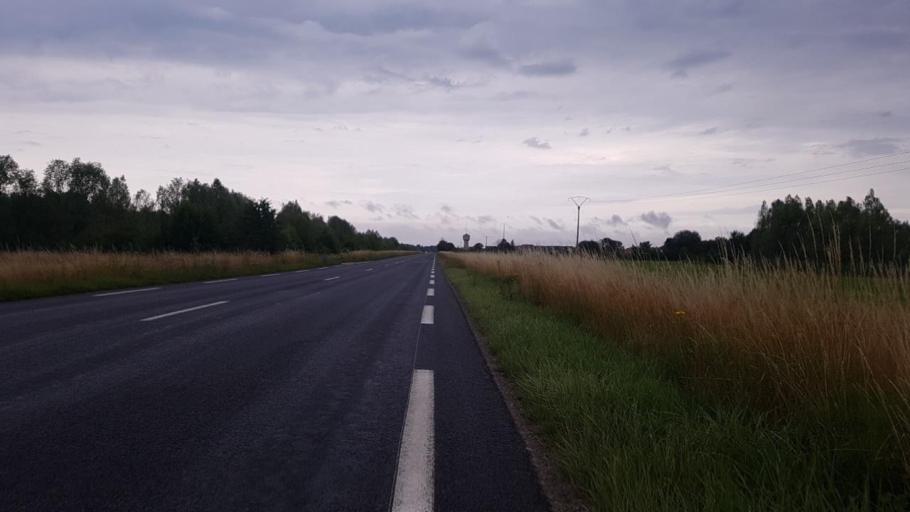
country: FR
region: Champagne-Ardenne
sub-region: Departement de la Marne
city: Vitry-le-Francois
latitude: 48.7449
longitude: 4.6831
